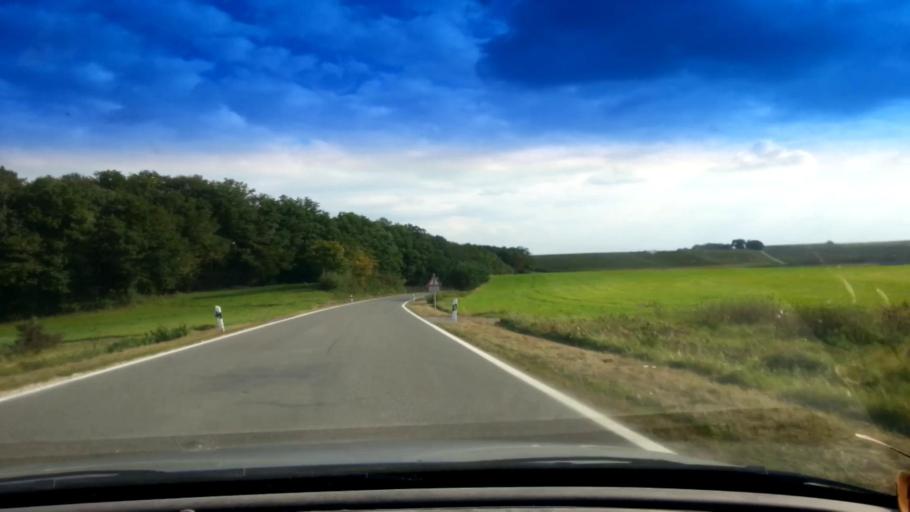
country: DE
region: Bavaria
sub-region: Upper Franconia
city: Zapfendorf
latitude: 49.9823
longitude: 10.9669
